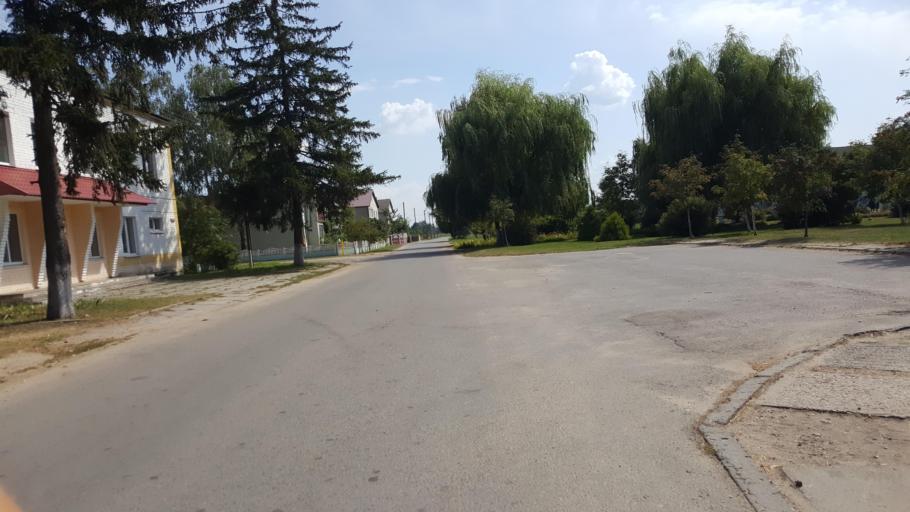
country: PL
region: Podlasie
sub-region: Powiat hajnowski
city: Czeremcha
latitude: 52.4978
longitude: 23.5693
